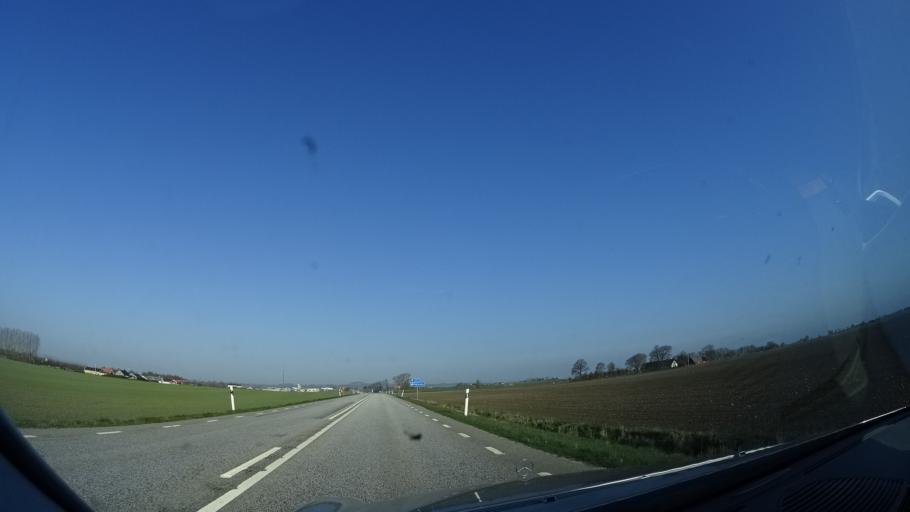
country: SE
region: Skane
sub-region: Svalovs Kommun
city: Teckomatorp
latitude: 55.8838
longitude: 13.0140
